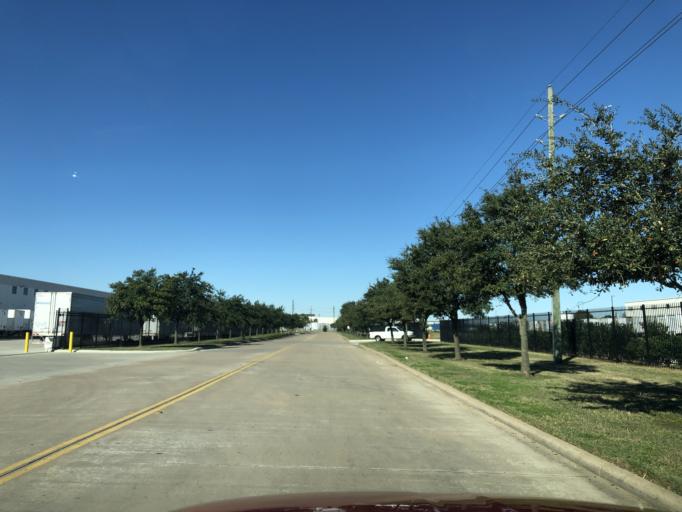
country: US
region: Texas
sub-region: Harris County
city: Oak Cliff Place
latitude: 29.9348
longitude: -95.6524
